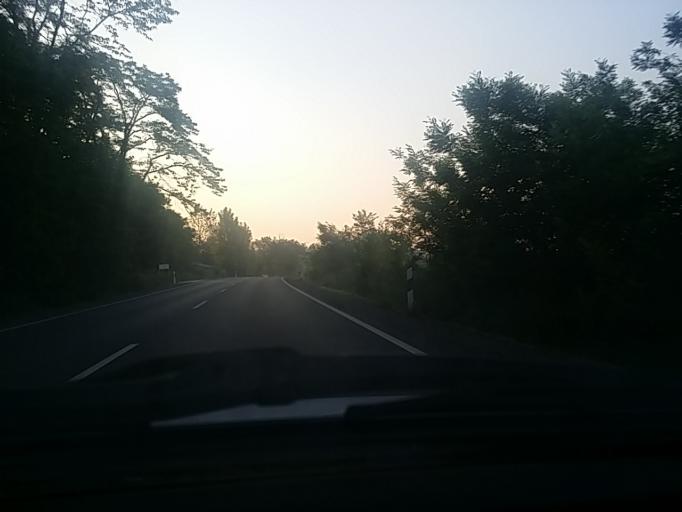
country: HU
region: Pest
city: Maglod
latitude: 47.4473
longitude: 19.3823
